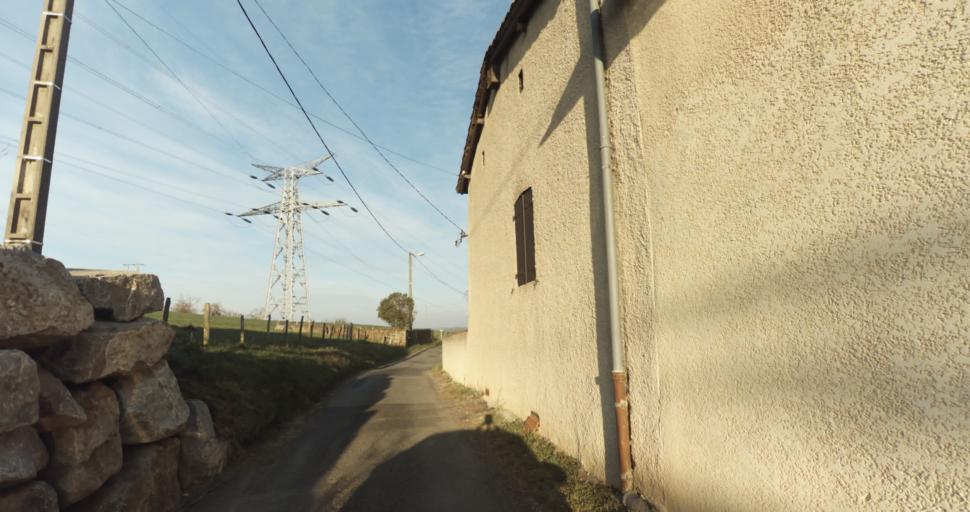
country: FR
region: Rhone-Alpes
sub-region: Departement de la Loire
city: Saint-Jean-Bonnefonds
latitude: 45.4564
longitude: 4.4397
